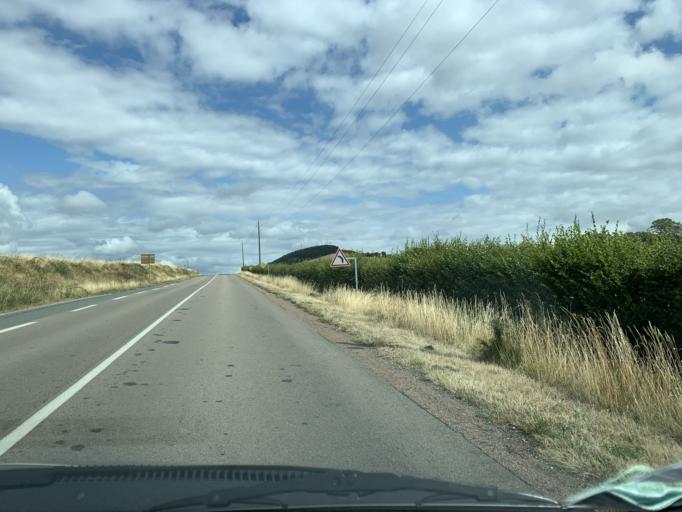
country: FR
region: Bourgogne
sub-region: Departement de la Nievre
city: Varzy
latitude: 47.3629
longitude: 3.4054
